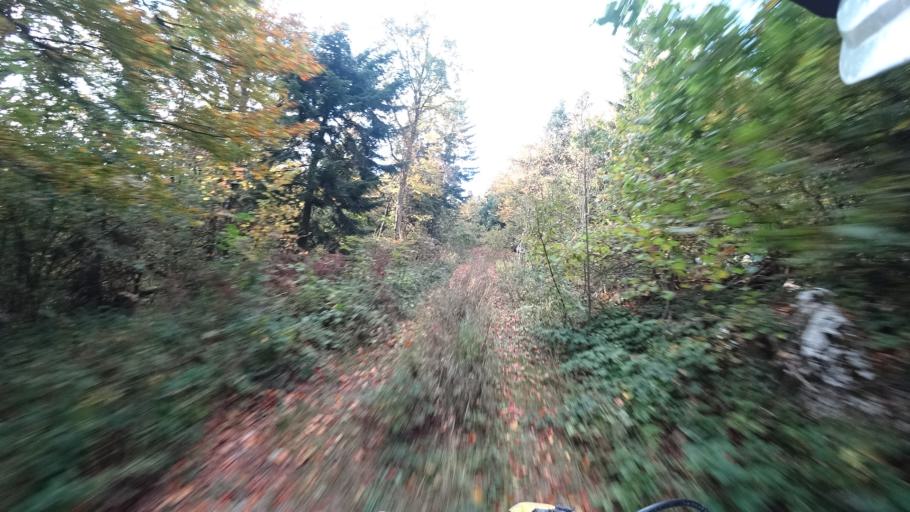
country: HR
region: Karlovacka
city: Plaski
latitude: 45.0272
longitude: 15.4320
